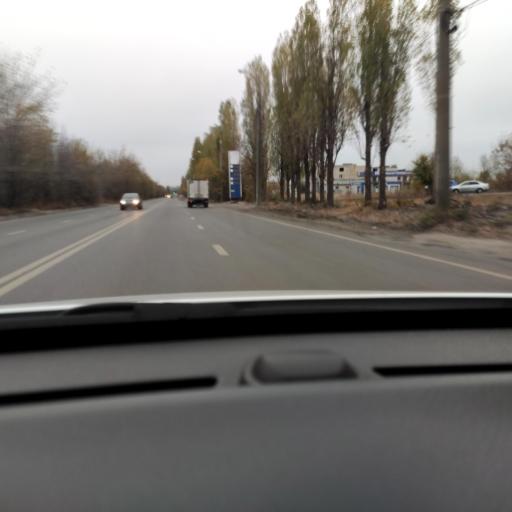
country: RU
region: Voronezj
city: Maslovka
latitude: 51.6054
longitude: 39.2548
